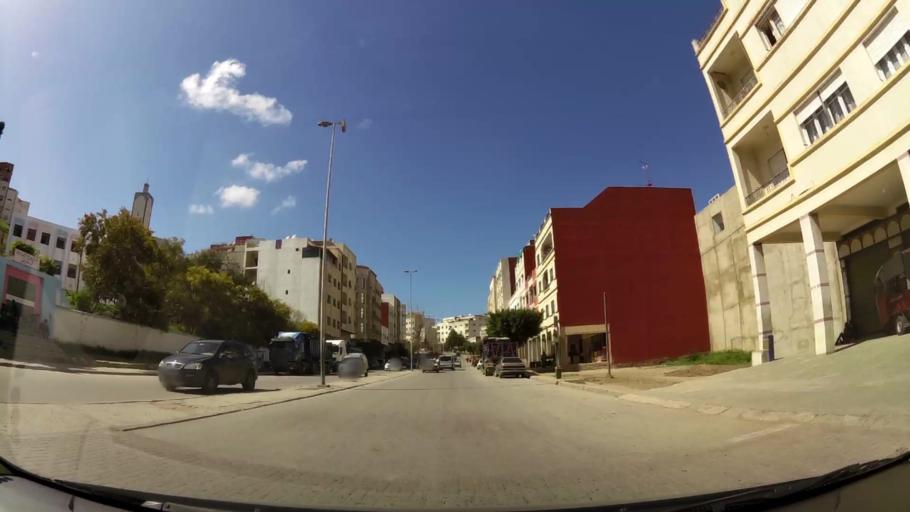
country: MA
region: Tanger-Tetouan
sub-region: Tanger-Assilah
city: Tangier
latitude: 35.7484
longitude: -5.8133
